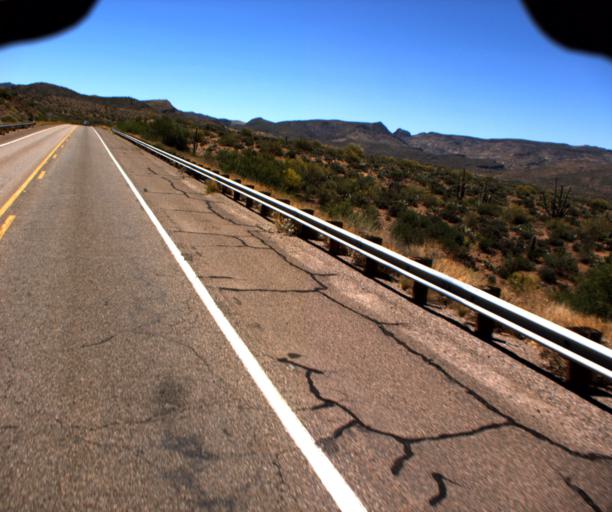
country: US
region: Arizona
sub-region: Pinal County
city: Superior
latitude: 33.2757
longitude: -111.0982
